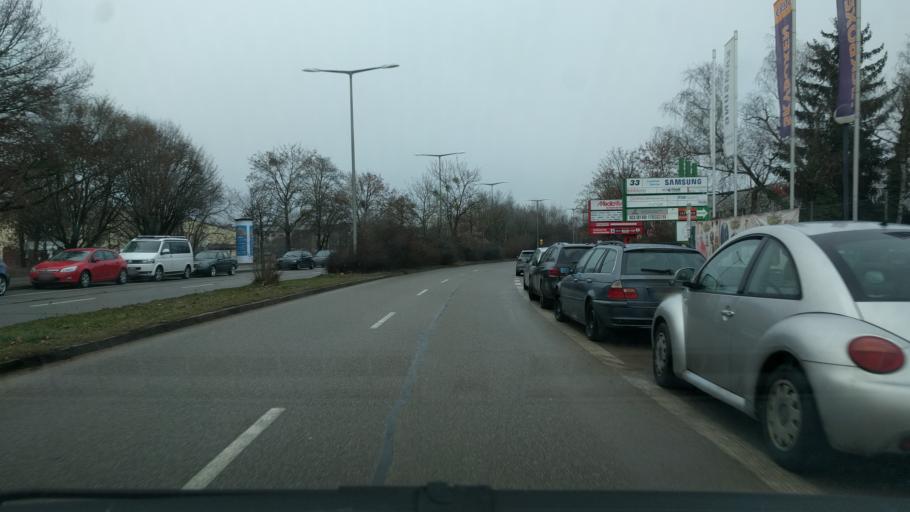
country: DE
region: Bavaria
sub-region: Upper Bavaria
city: Pullach im Isartal
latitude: 48.0923
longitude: 11.5029
